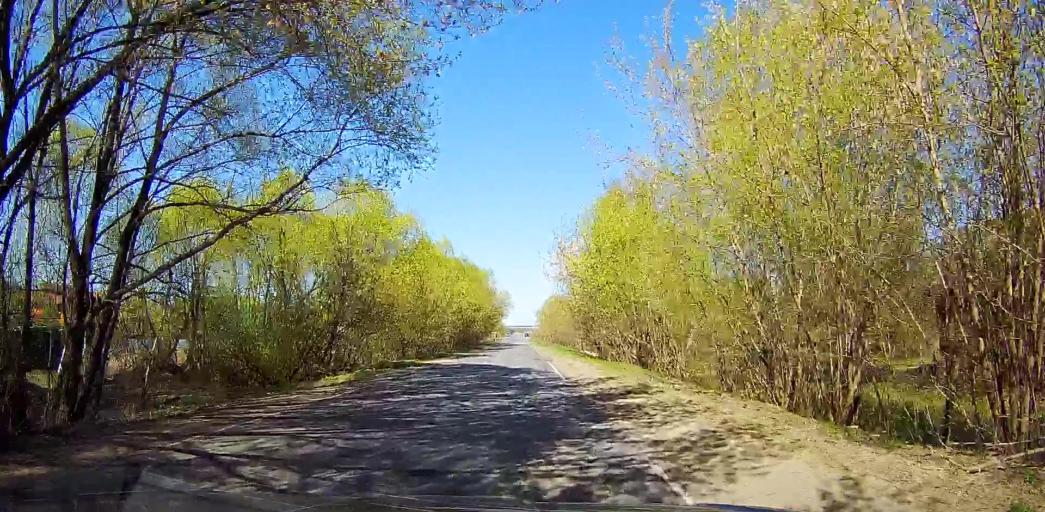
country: RU
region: Moskovskaya
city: Bronnitsy
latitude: 55.4845
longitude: 38.2366
